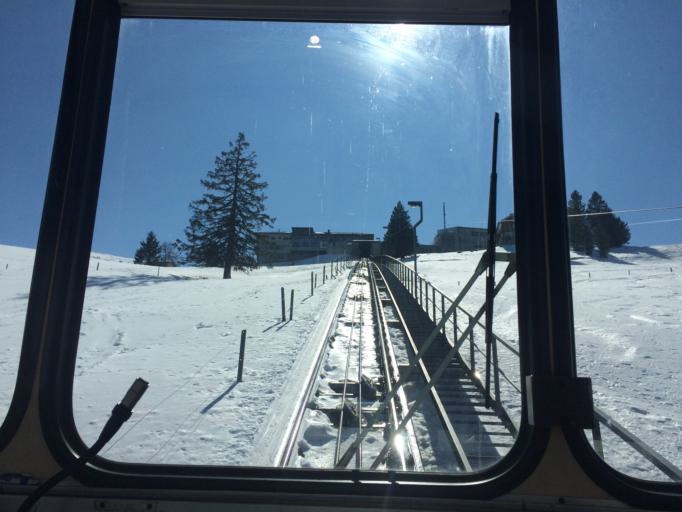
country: CH
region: Saint Gallen
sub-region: Wahlkreis Toggenburg
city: Wildhaus
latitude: 47.1869
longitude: 9.3126
